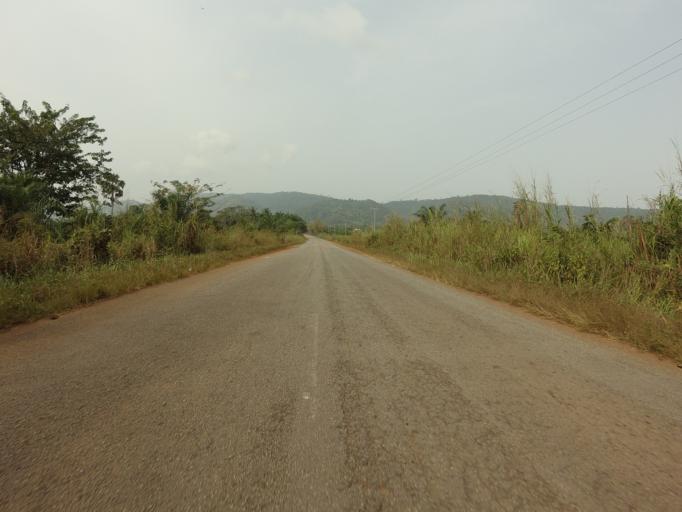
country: GH
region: Volta
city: Ho
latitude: 6.5750
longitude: 0.3200
